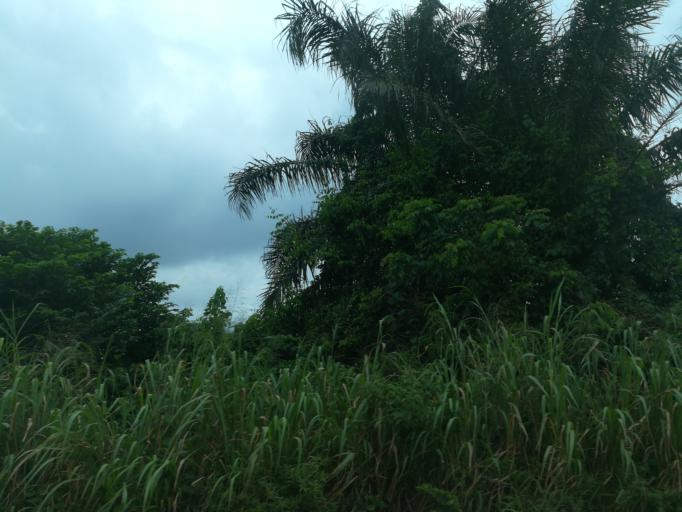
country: NG
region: Lagos
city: Ejirin
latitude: 6.6454
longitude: 3.7282
